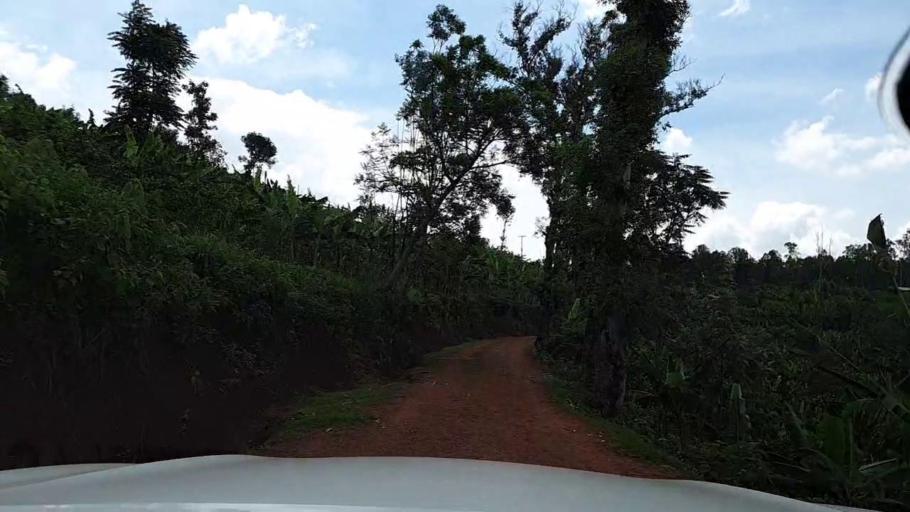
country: RW
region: Southern Province
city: Butare
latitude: -2.7515
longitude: 29.7619
